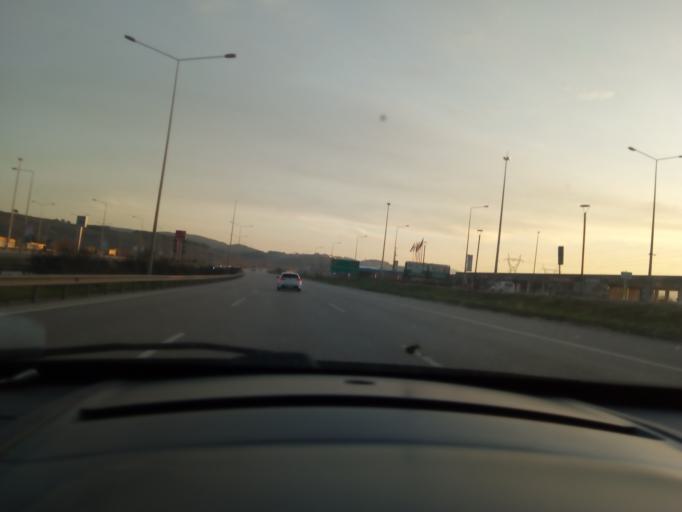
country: TR
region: Bursa
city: Niluefer
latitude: 40.2814
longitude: 28.9943
